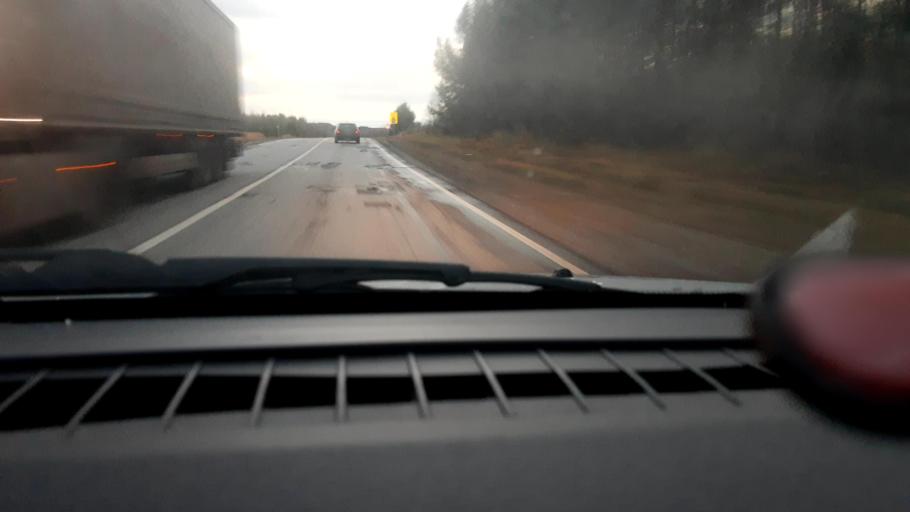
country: RU
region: Nizjnij Novgorod
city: Krasnyye Baki
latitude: 56.9832
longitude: 45.1171
